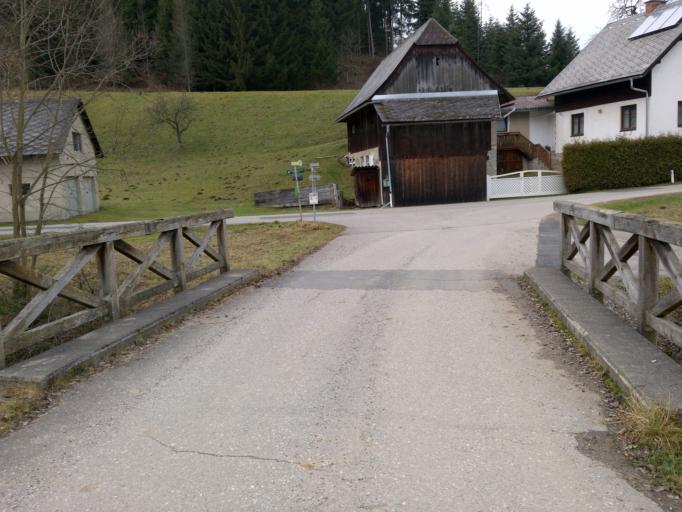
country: AT
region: Styria
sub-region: Politischer Bezirk Murtal
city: Grosslobming
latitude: 47.1442
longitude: 14.7816
